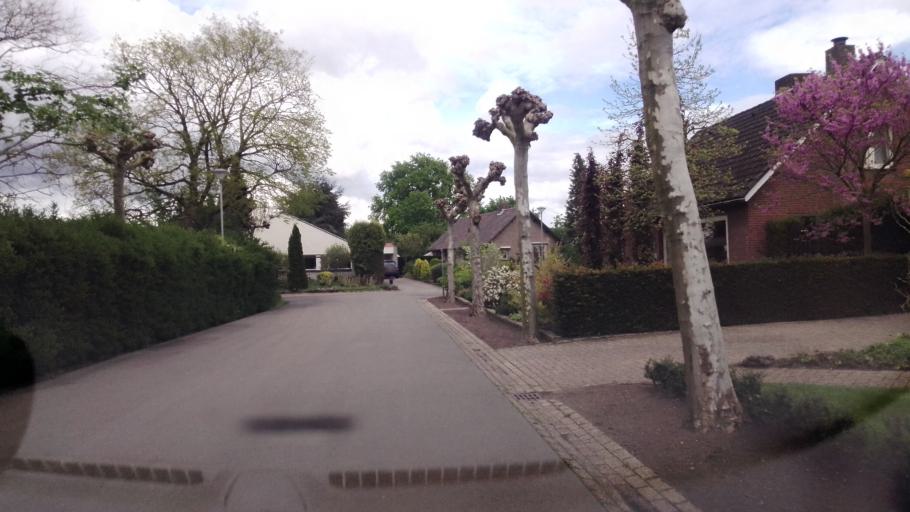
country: NL
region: Limburg
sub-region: Gemeente Bergen
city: Wellerlooi
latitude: 51.4907
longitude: 6.1188
